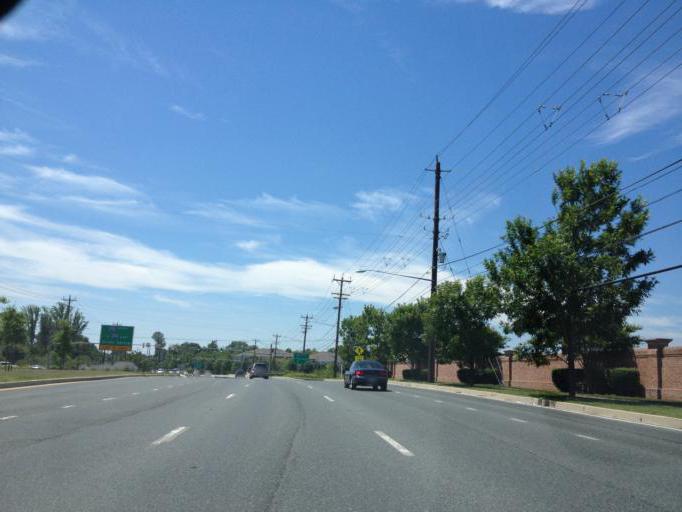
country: US
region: Maryland
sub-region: Montgomery County
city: North Bethesda
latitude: 39.0326
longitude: -77.1260
